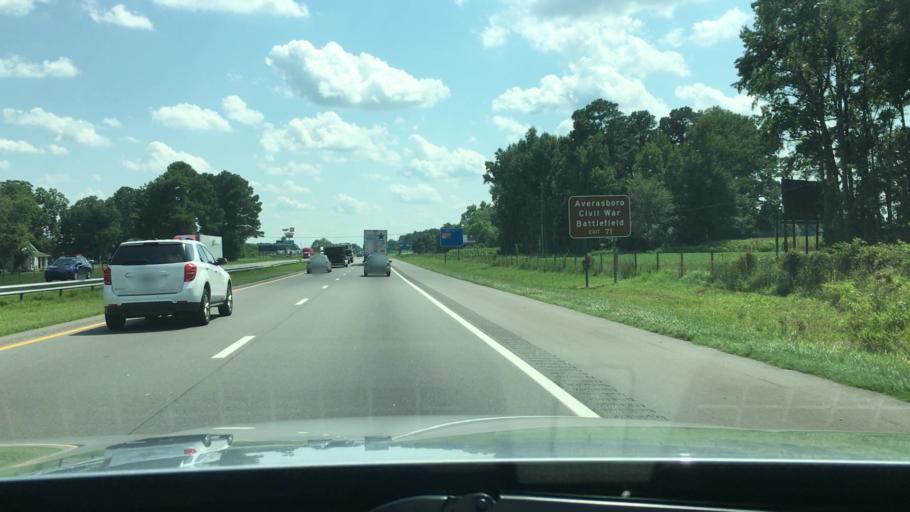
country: US
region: North Carolina
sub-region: Harnett County
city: Dunn
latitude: 35.2782
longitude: -78.6126
